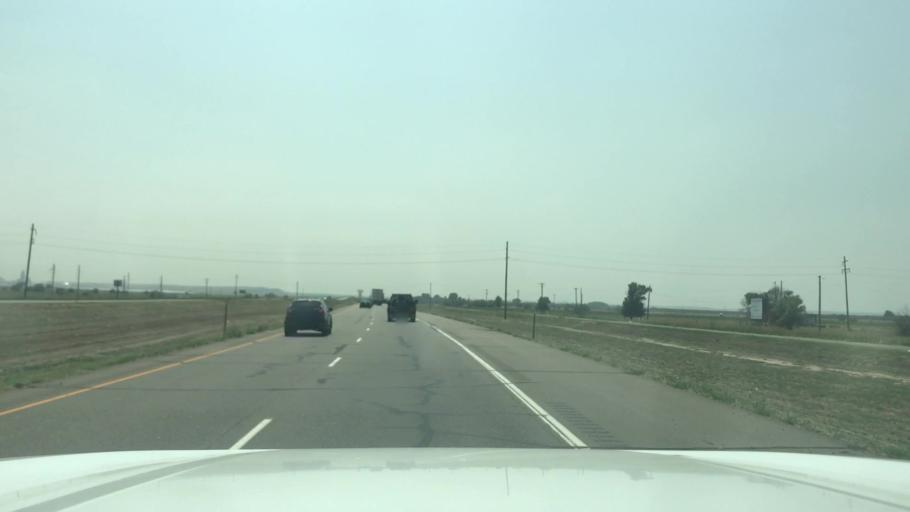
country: US
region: Colorado
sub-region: Pueblo County
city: Pueblo
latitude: 38.1966
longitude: -104.6327
